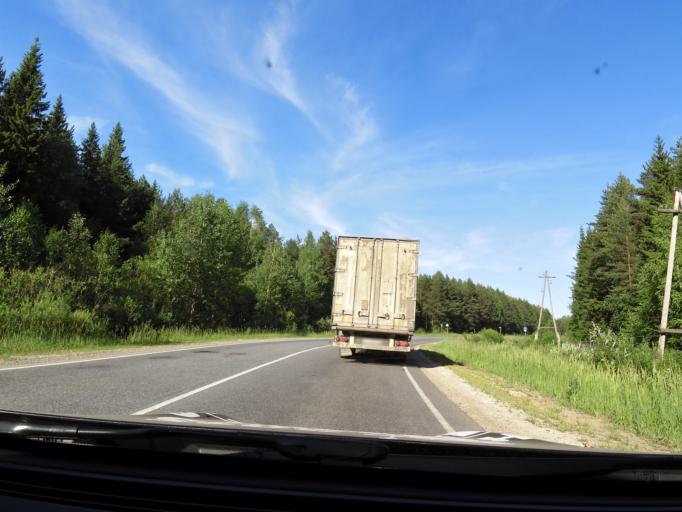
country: RU
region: Kirov
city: Belaya Kholunitsa
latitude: 58.8725
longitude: 50.8505
